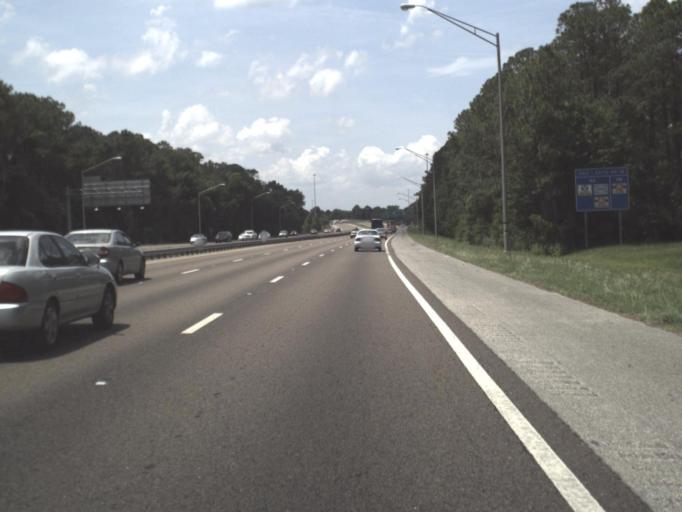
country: US
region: Florida
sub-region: Saint Johns County
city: Fruit Cove
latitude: 30.1760
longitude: -81.6200
